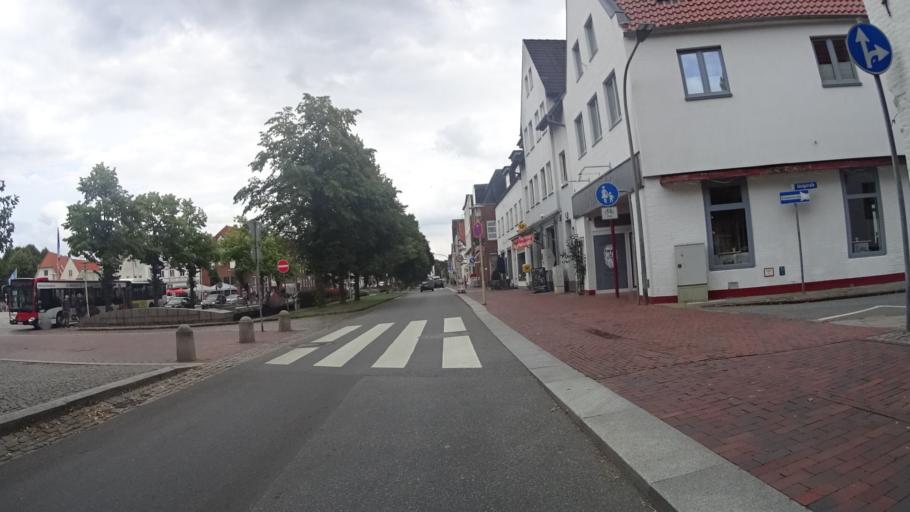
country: DE
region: Schleswig-Holstein
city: Gluckstadt
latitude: 53.7880
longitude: 9.4228
